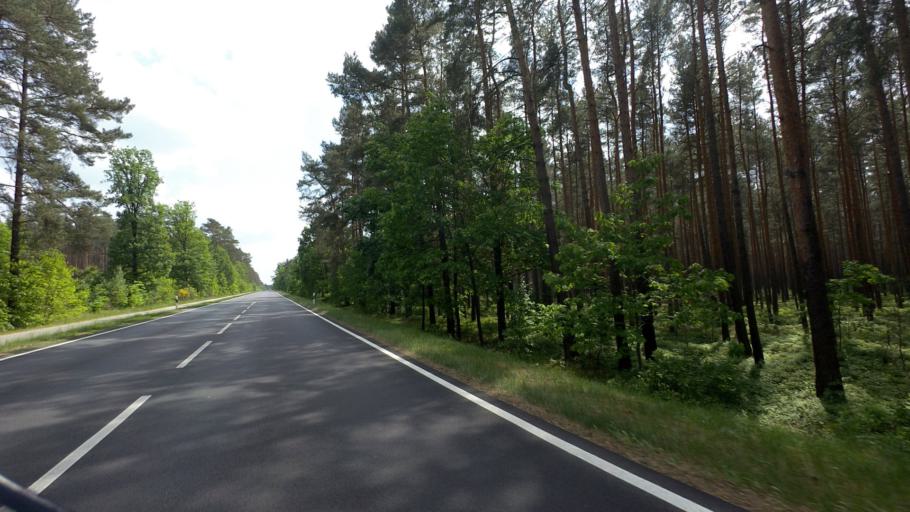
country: DE
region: Saxony
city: Niesky
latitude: 51.3445
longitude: 14.8053
